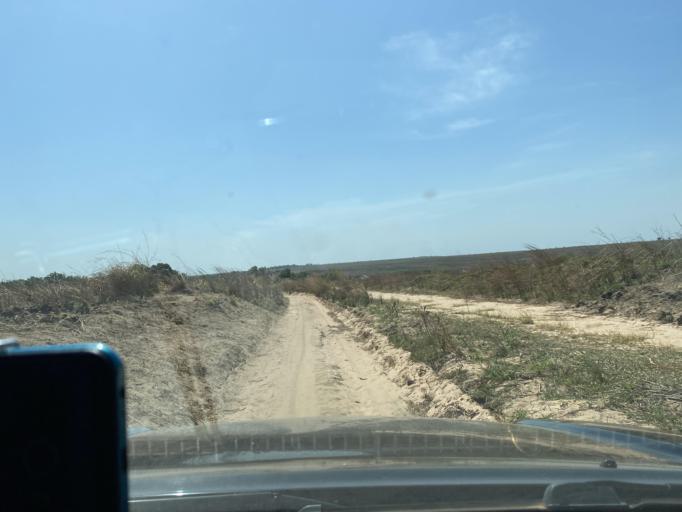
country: CD
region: Kasai-Oriental
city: Kabinda
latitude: -5.9123
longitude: 24.8501
